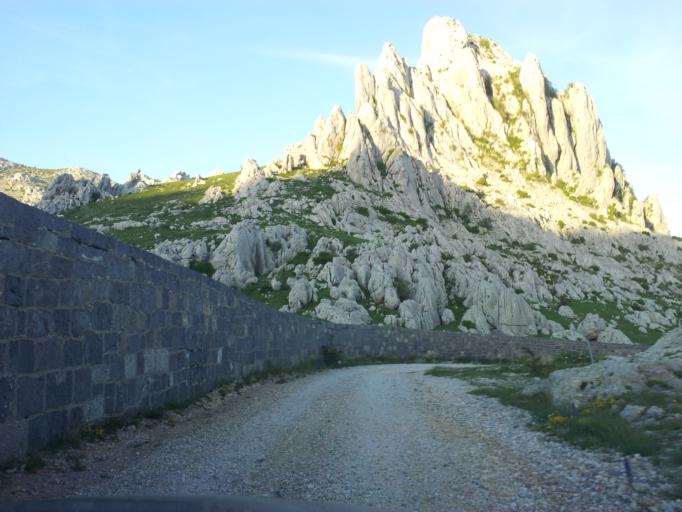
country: HR
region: Zadarska
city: Obrovac
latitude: 44.2638
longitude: 15.6470
